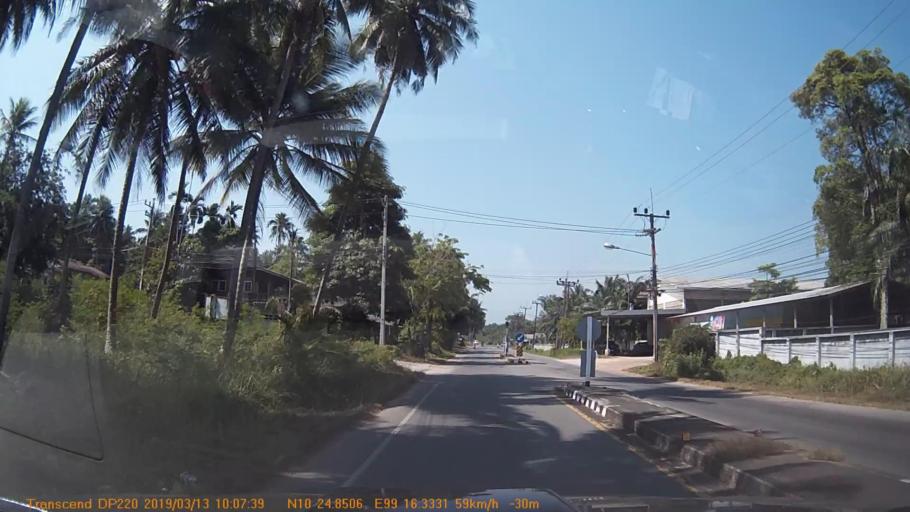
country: TH
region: Chumphon
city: Chumphon
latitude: 10.4141
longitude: 99.2722
